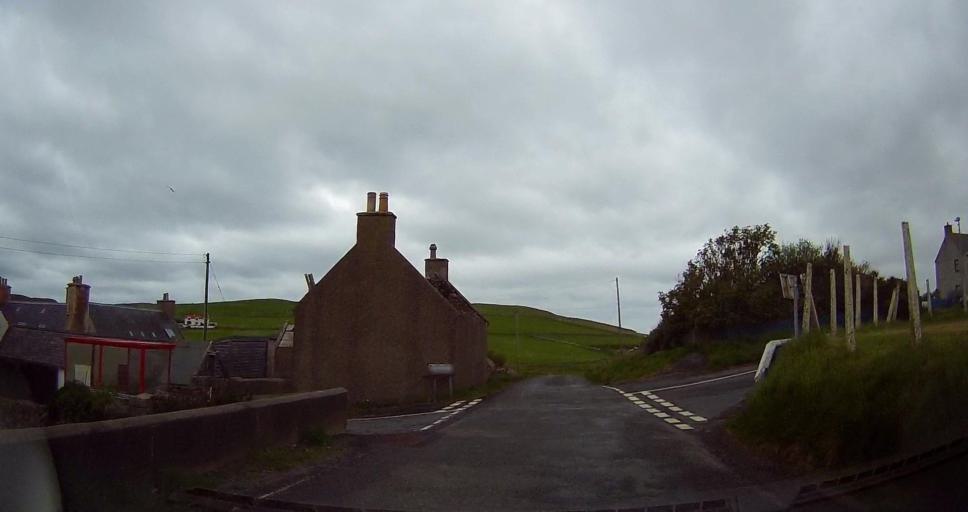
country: GB
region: Scotland
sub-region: Shetland Islands
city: Lerwick
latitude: 60.4766
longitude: -1.4880
